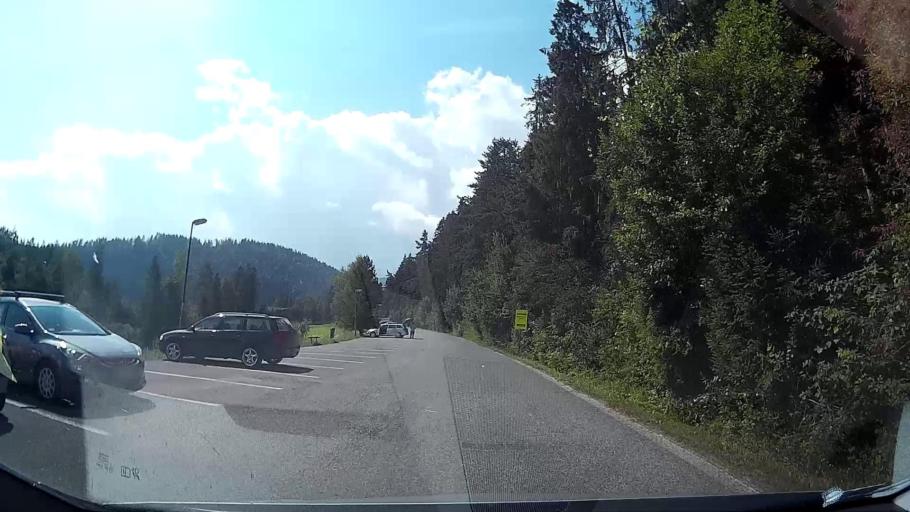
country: SK
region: Kosicky
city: Spisska Nova Ves
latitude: 48.9455
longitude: 20.4849
